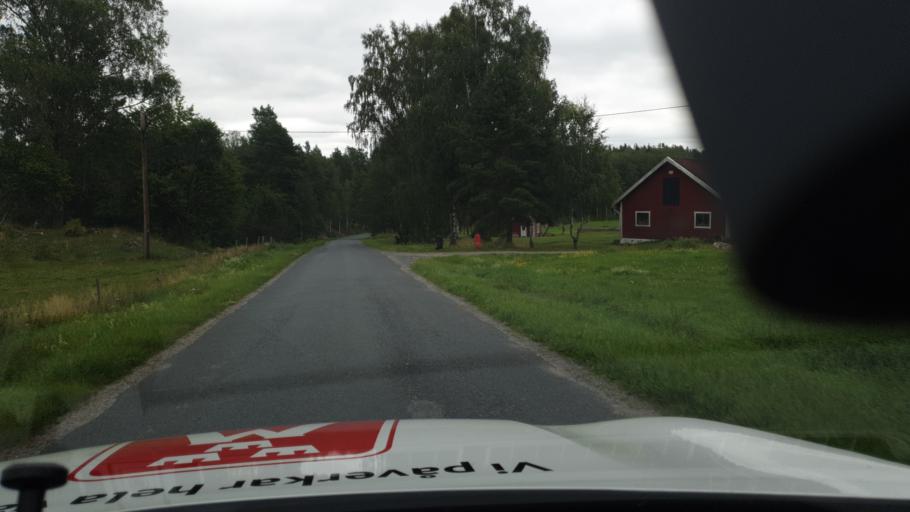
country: SE
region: Soedermanland
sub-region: Strangnas Kommun
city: Mariefred
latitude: 59.1770
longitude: 17.1677
